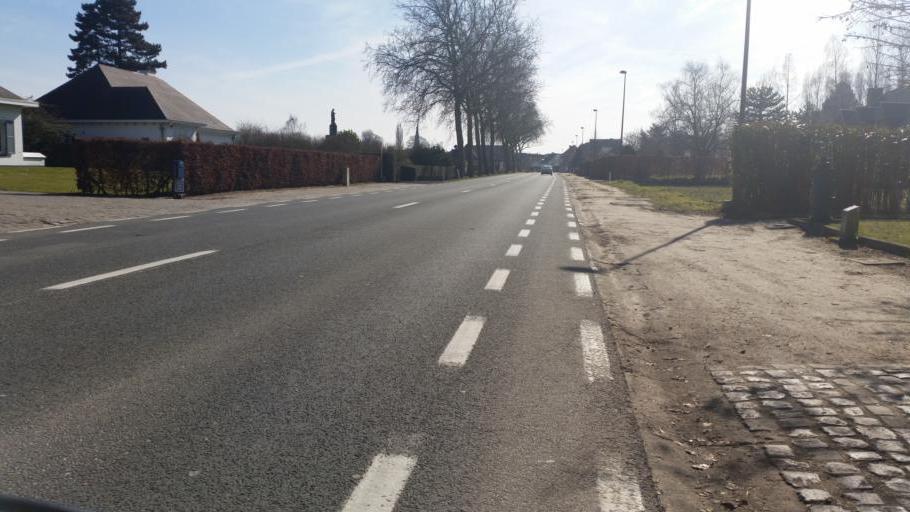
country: BE
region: Flanders
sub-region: Provincie Vlaams-Brabant
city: Steenokkerzeel
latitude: 50.9394
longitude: 4.4945
